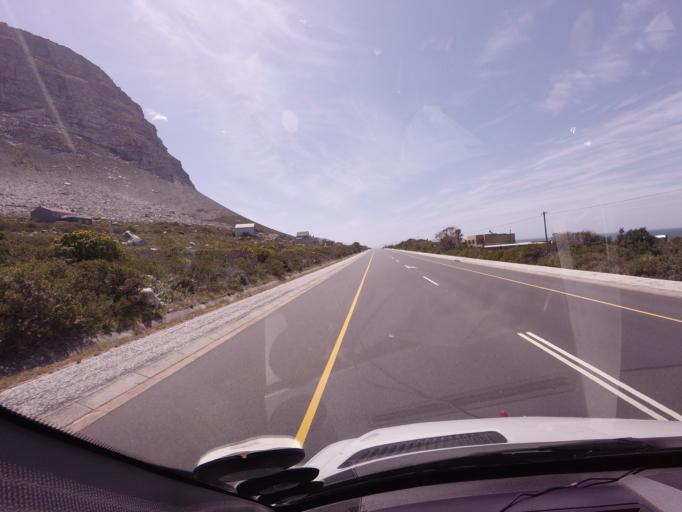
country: ZA
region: Western Cape
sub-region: Overberg District Municipality
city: Grabouw
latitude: -34.3576
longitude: 18.9559
